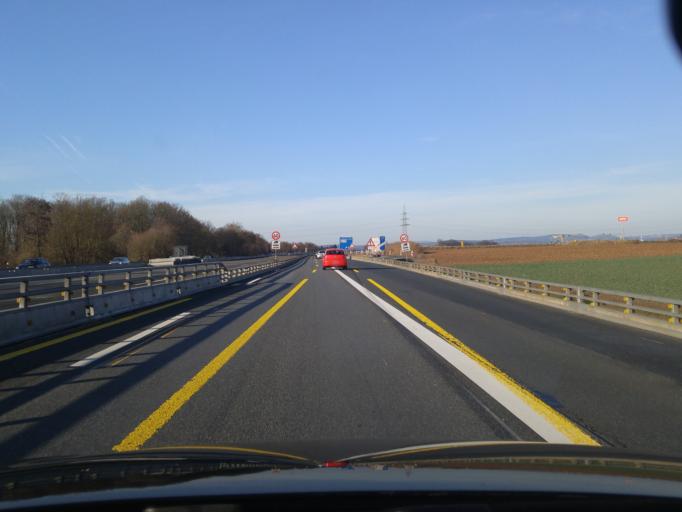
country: DE
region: Hesse
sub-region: Regierungsbezirk Giessen
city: Limburg an der Lahn
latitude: 50.3776
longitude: 8.0930
